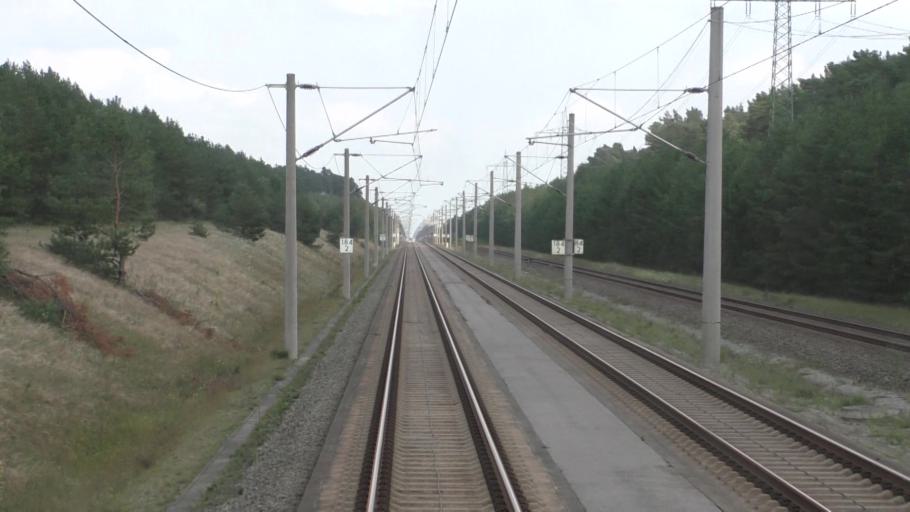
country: DE
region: Saxony-Anhalt
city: Schollene
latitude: 52.5903
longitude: 12.1579
